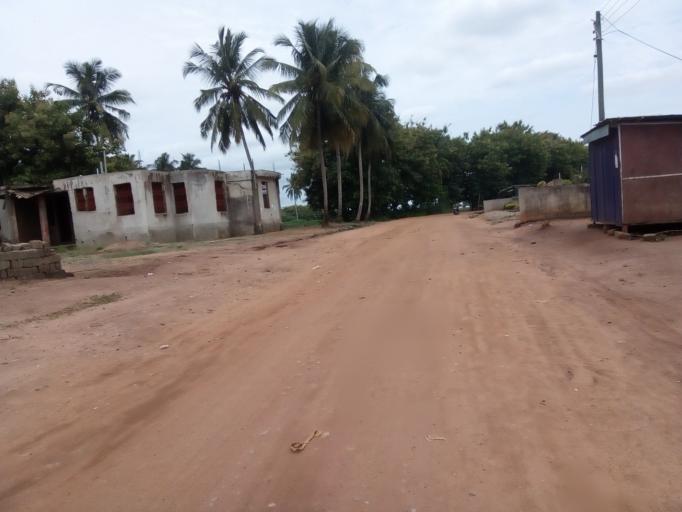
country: GH
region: Eastern
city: Nsawam
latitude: 5.7781
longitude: -0.3395
